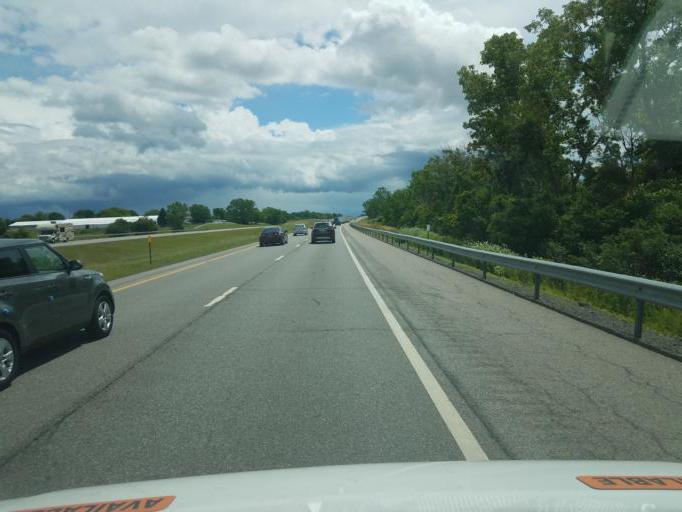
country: US
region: New York
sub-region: Monroe County
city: Pittsford
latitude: 43.0447
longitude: -77.5595
